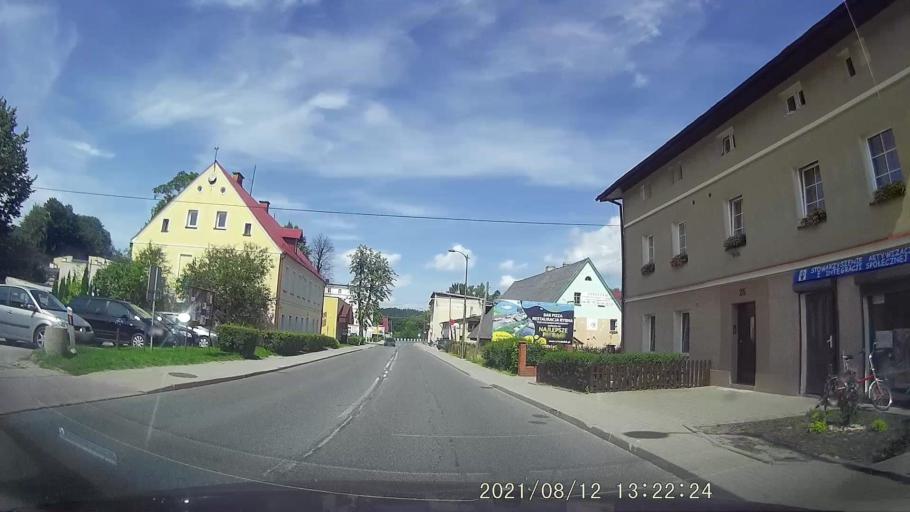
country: PL
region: Lower Silesian Voivodeship
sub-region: Powiat klodzki
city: Stronie Slaskie
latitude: 50.2982
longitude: 16.8738
